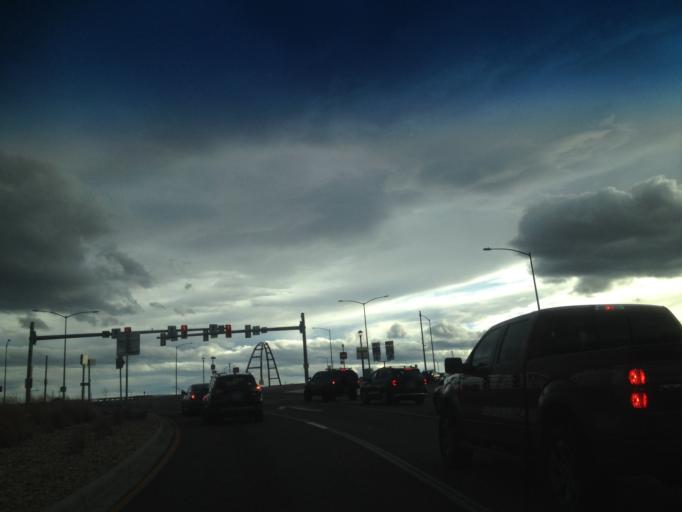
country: US
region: Colorado
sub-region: Boulder County
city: Superior
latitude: 39.9594
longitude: -105.1655
